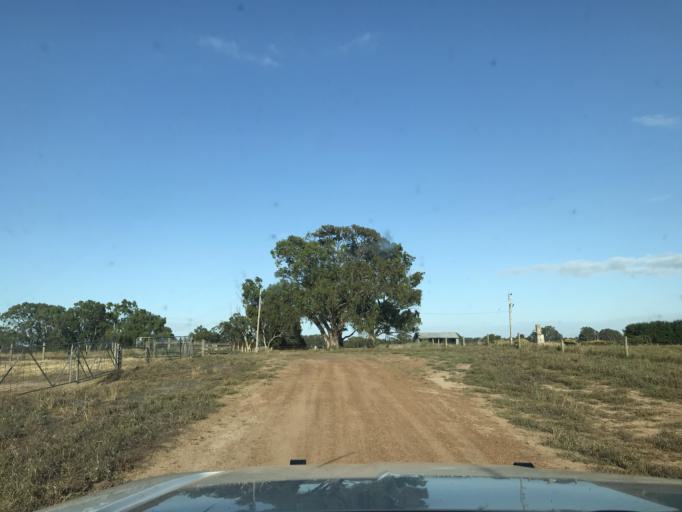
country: AU
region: South Australia
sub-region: Naracoorte and Lucindale
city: Naracoorte
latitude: -36.9548
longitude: 141.3592
